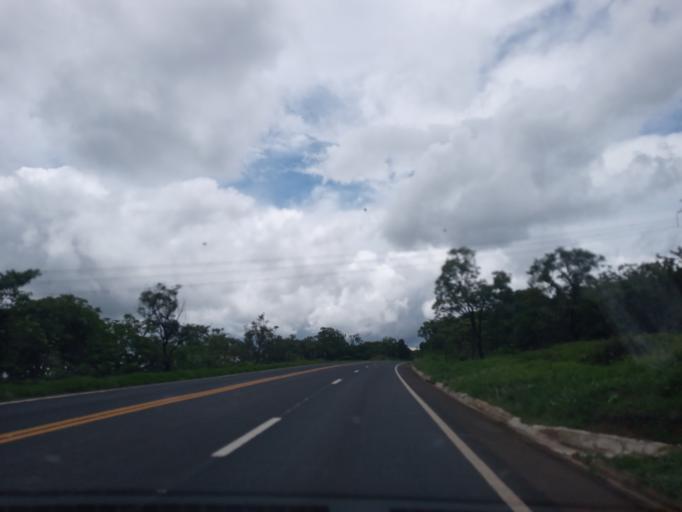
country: BR
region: Minas Gerais
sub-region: Uberaba
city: Uberaba
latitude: -19.2703
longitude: -47.6655
